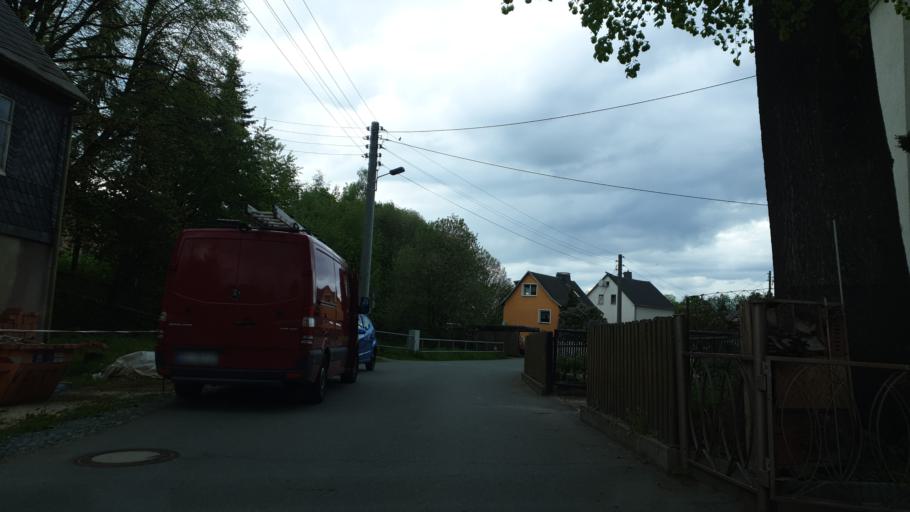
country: DE
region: Saxony
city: Gersdorf
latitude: 50.7457
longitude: 12.7260
